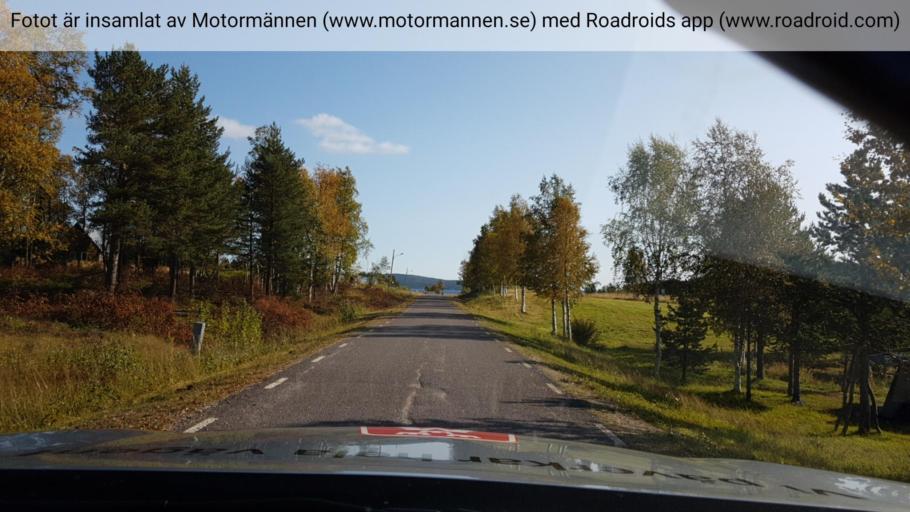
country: SE
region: Norrbotten
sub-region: Jokkmokks Kommun
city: Jokkmokk
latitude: 67.1244
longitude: 19.4958
